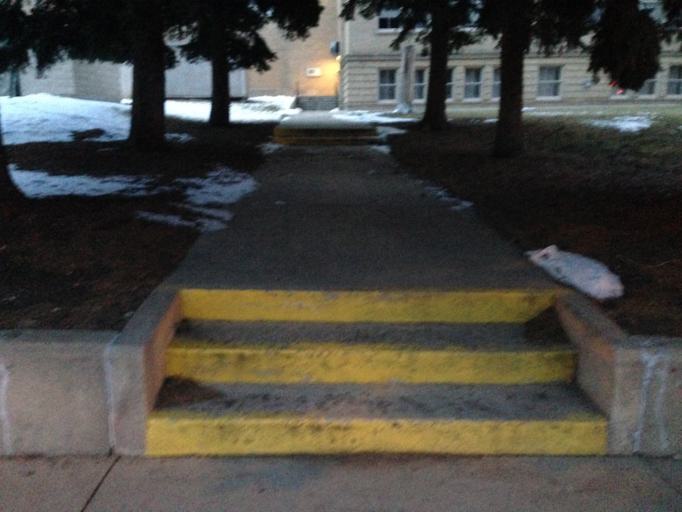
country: US
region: Colorado
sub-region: Jefferson County
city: Golden
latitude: 39.7580
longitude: -105.2236
